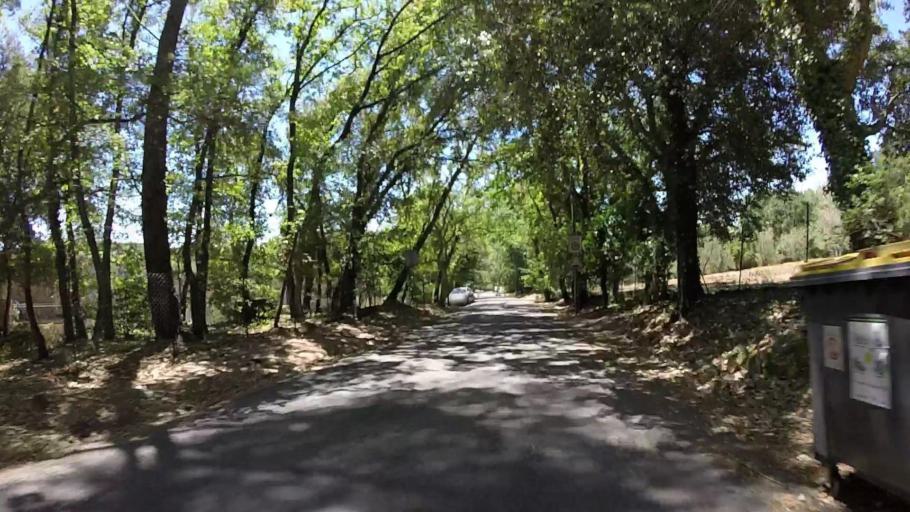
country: FR
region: Provence-Alpes-Cote d'Azur
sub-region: Departement des Alpes-Maritimes
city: Valbonne
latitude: 43.6285
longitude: 7.0150
